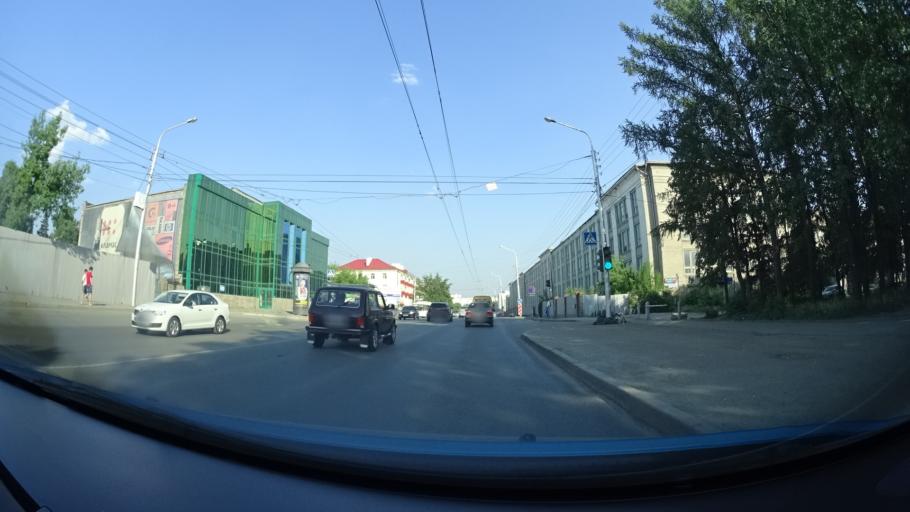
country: RU
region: Bashkortostan
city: Ufa
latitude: 54.7533
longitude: 56.0107
